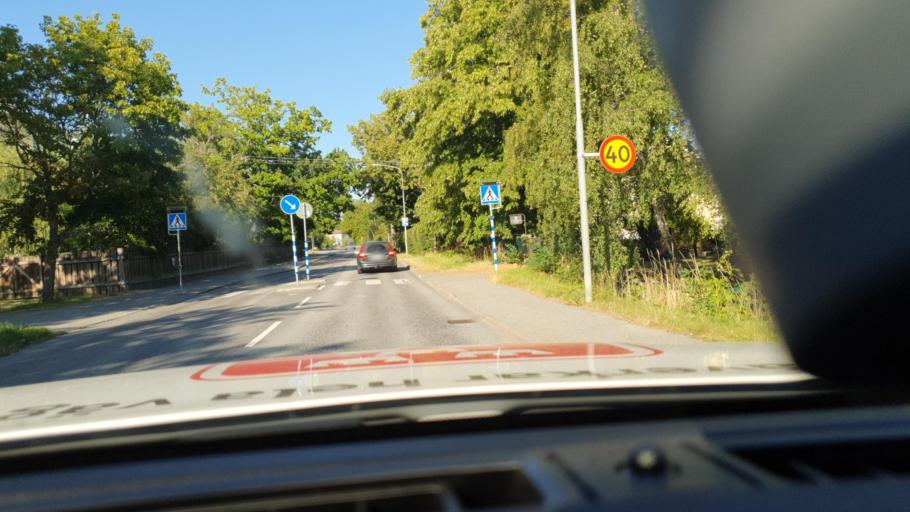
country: SE
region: Stockholm
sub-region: Danderyds Kommun
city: Djursholm
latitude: 59.3829
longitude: 18.0553
